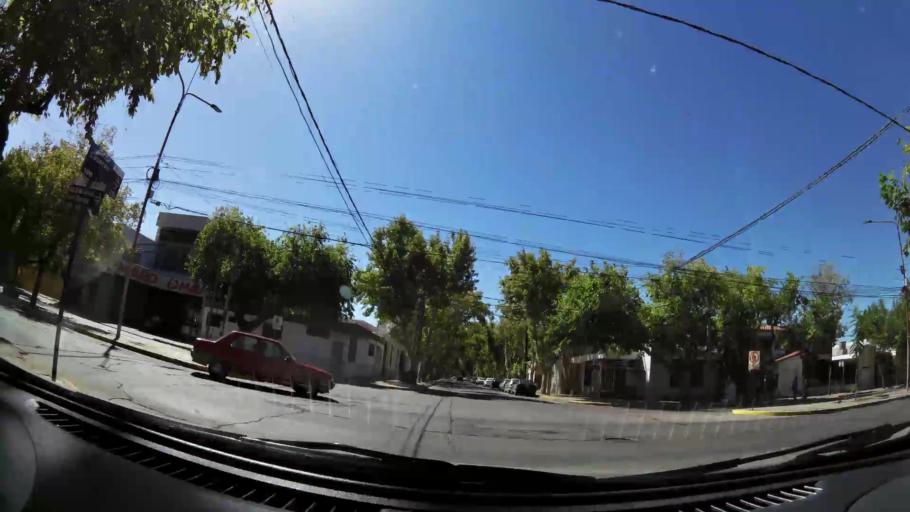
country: AR
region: San Juan
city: San Juan
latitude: -31.5337
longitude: -68.5176
